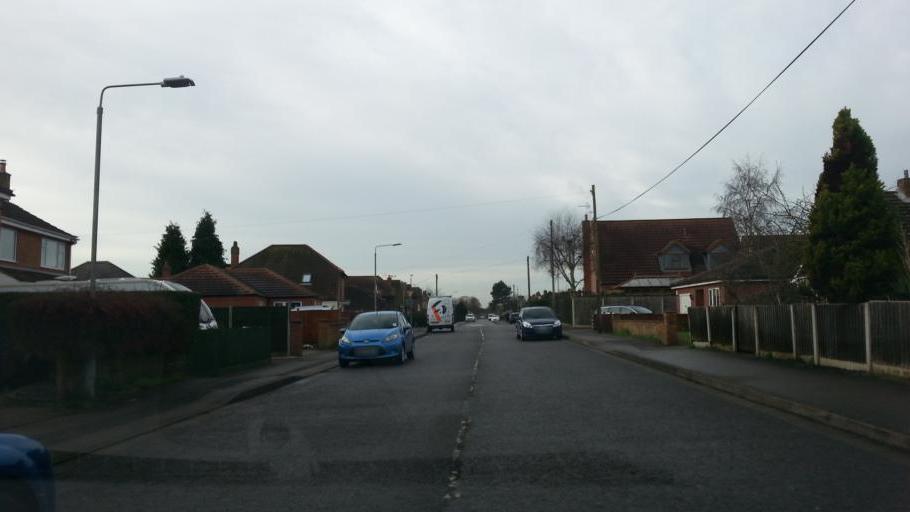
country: GB
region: England
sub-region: Nottinghamshire
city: Farndon
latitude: 53.0638
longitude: -0.8432
